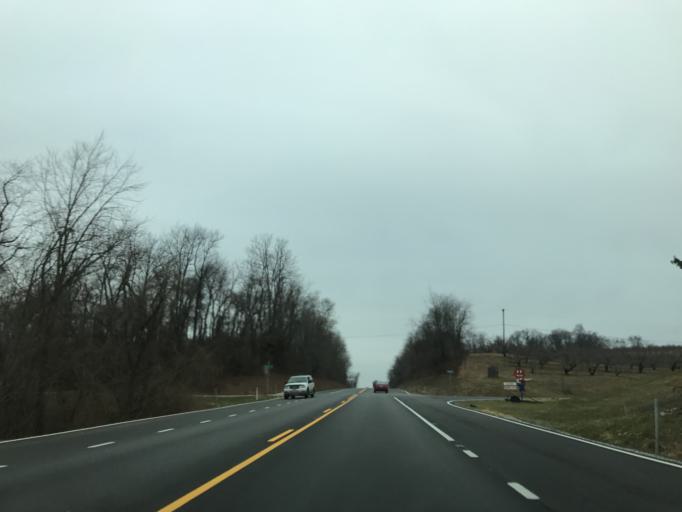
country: US
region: Maryland
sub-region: Carroll County
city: Westminster
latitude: 39.6013
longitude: -77.0502
